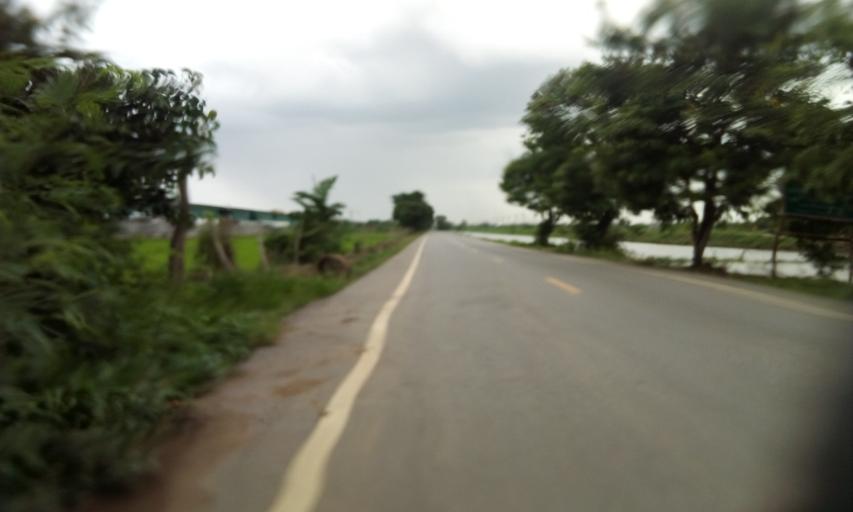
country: TH
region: Pathum Thani
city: Nong Suea
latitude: 14.0761
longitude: 100.8467
